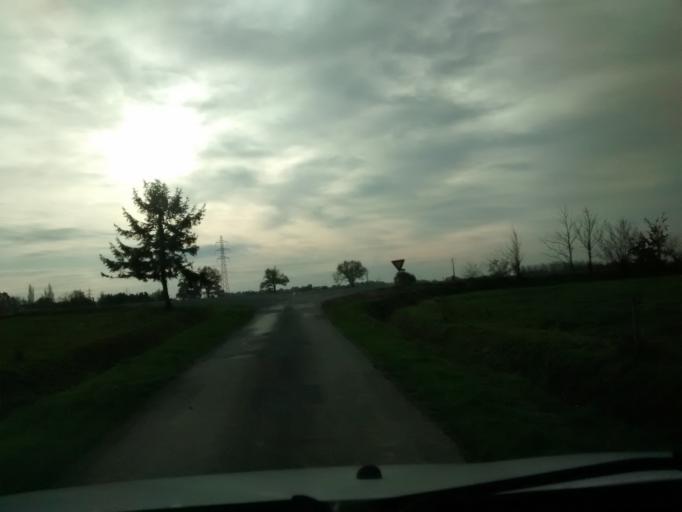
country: FR
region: Brittany
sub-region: Departement d'Ille-et-Vilaine
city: Cesson-Sevigne
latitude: 48.0990
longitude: -1.5703
